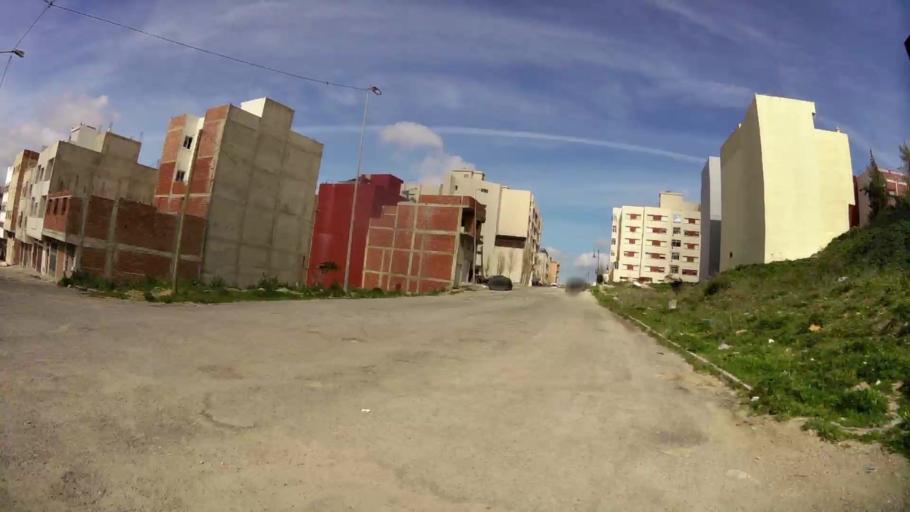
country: MA
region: Tanger-Tetouan
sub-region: Tanger-Assilah
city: Tangier
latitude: 35.7667
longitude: -5.7737
